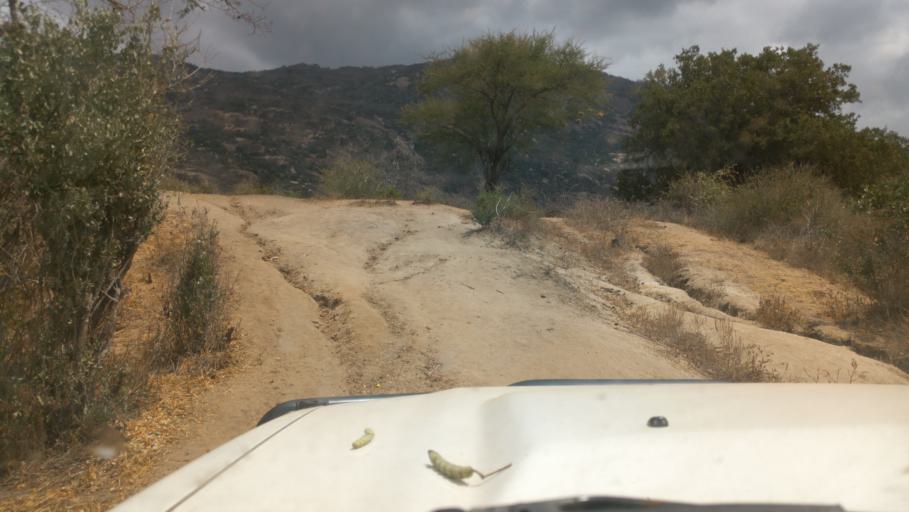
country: KE
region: Kitui
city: Kitui
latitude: -1.8839
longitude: 38.3683
